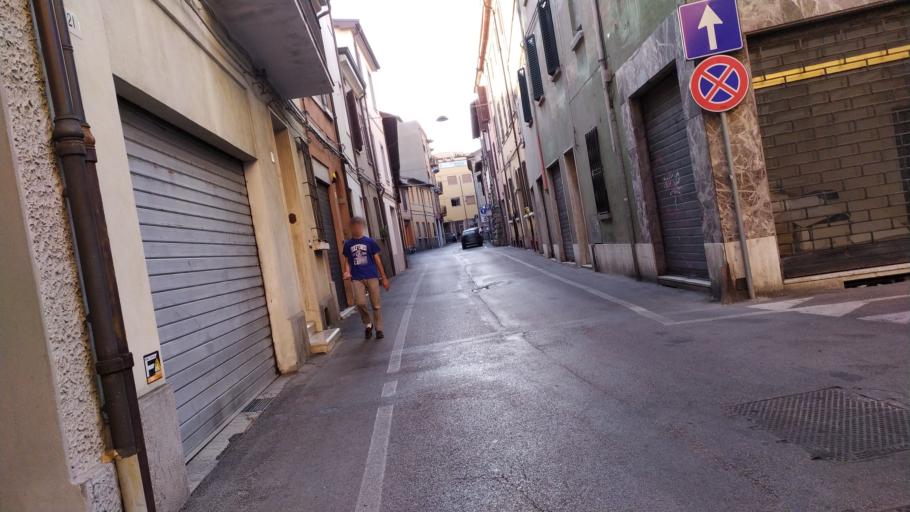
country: IT
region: Emilia-Romagna
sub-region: Forli-Cesena
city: Forli
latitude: 44.2248
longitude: 12.0428
